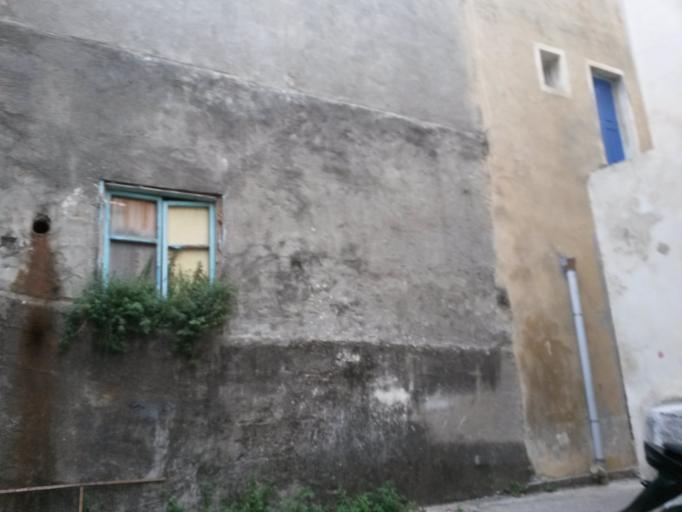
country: GR
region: North Aegean
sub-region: Nomos Lesvou
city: Plomarion
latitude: 38.9762
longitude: 26.3696
